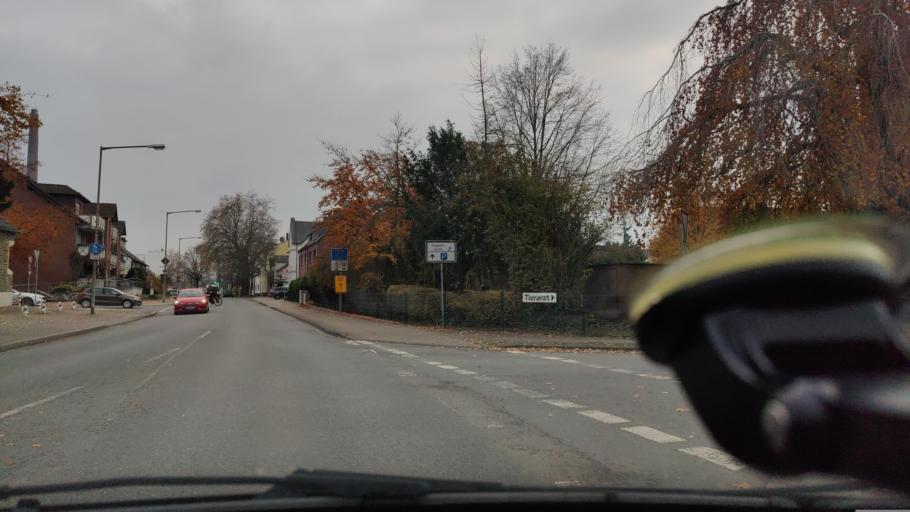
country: DE
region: North Rhine-Westphalia
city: Lunen
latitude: 51.6284
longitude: 7.5109
